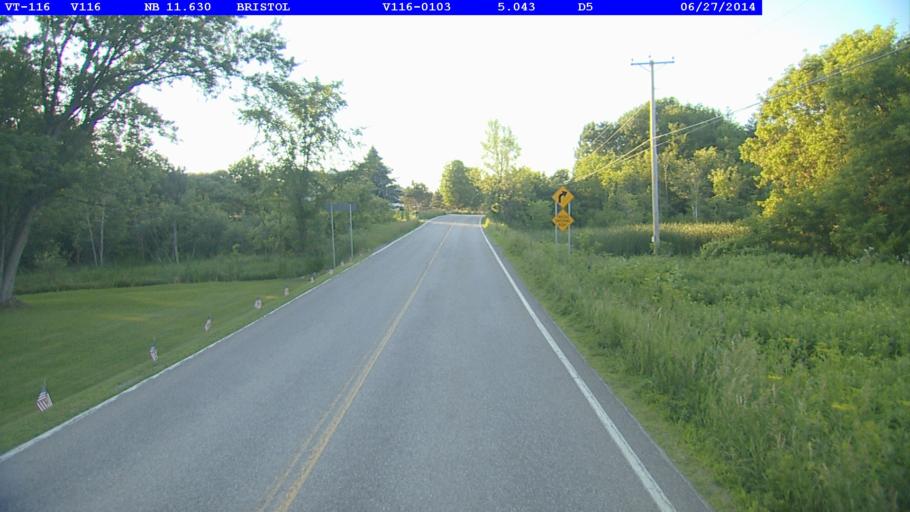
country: US
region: Vermont
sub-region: Addison County
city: Bristol
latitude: 44.1230
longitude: -73.0972
